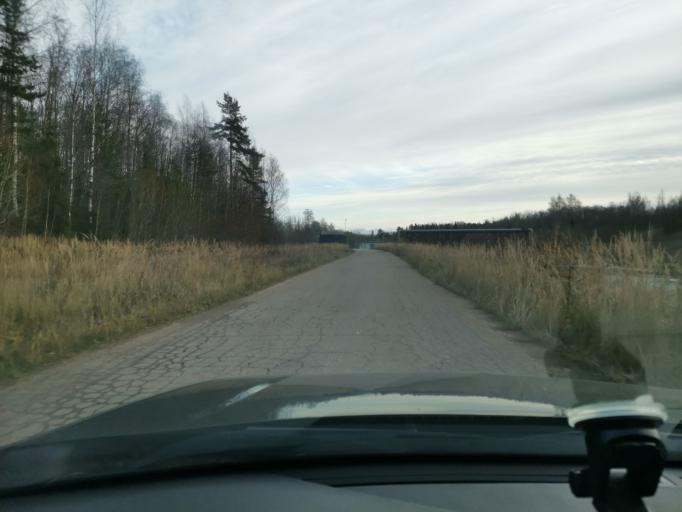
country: EE
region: Ida-Virumaa
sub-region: Sillamaee linn
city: Sillamae
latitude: 59.2615
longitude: 27.9073
